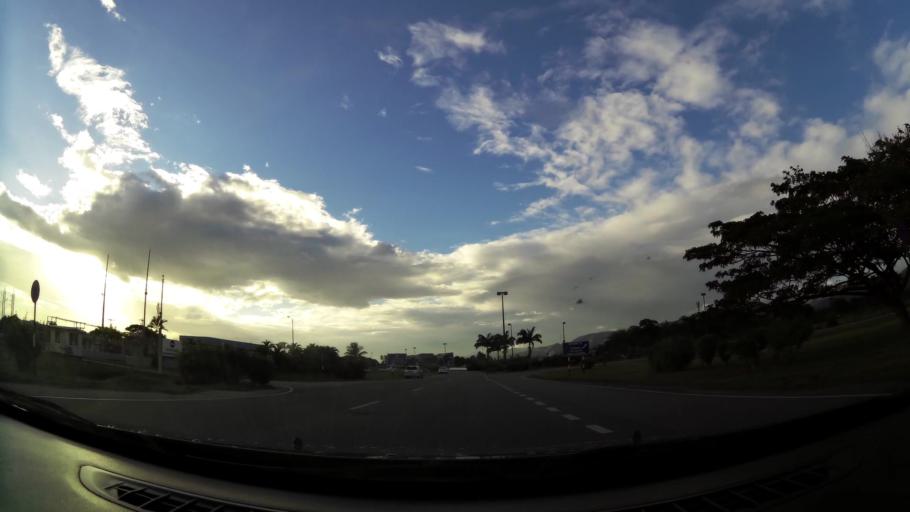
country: TT
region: Tunapuna/Piarco
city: Arouca
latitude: 10.6036
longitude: -61.3426
